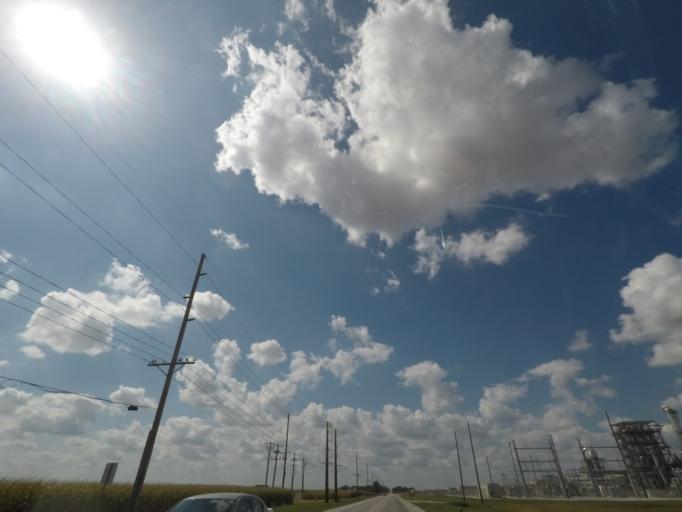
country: US
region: Iowa
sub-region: Story County
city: Nevada
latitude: 42.0231
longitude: -93.5133
